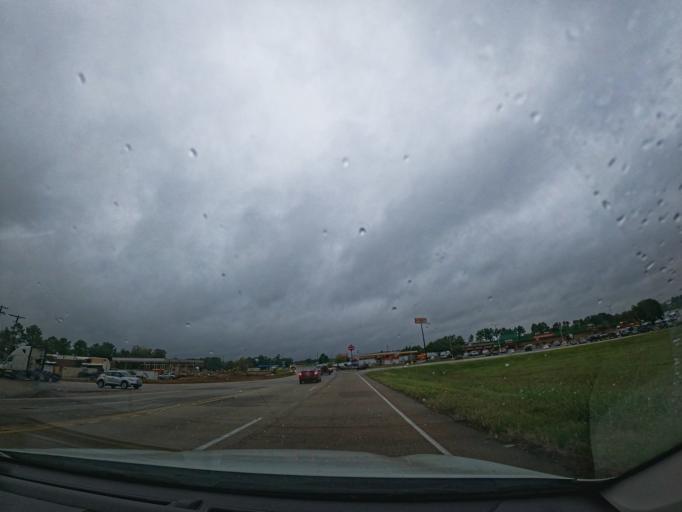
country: US
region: Louisiana
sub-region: Caddo Parish
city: Greenwood
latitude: 32.4457
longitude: -93.8998
